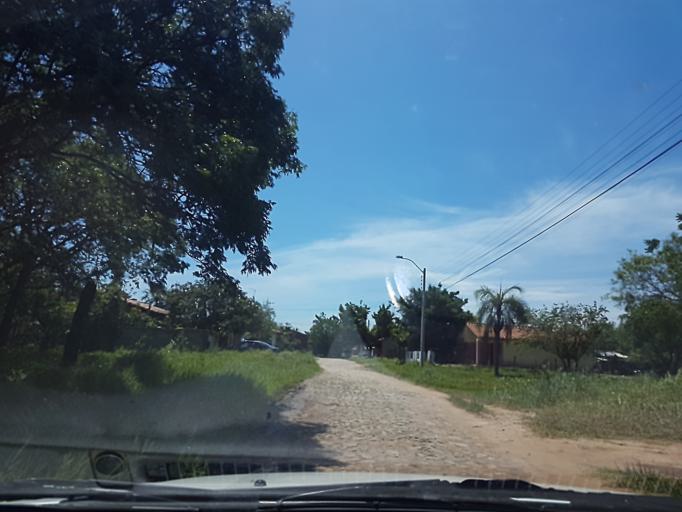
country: PY
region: Central
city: Limpio
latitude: -25.1832
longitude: -57.4885
